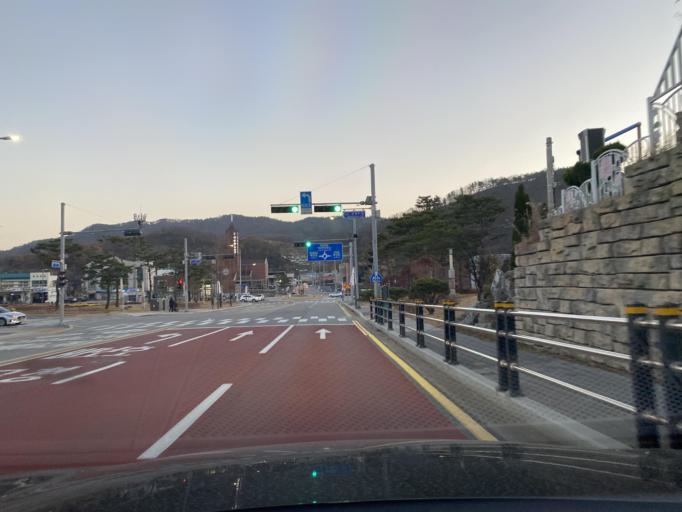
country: KR
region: Chungcheongnam-do
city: Yesan
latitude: 36.6798
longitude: 126.8434
